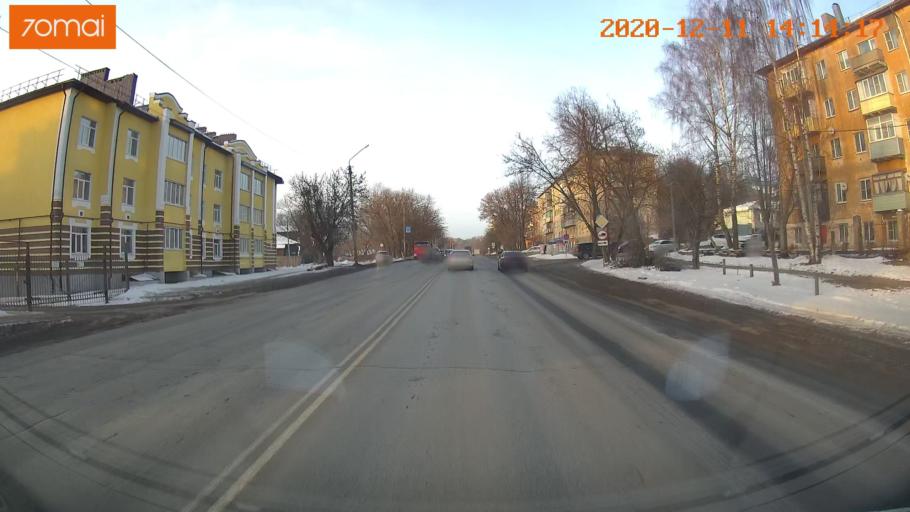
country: RU
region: Kostroma
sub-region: Kostromskoy Rayon
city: Kostroma
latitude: 57.7516
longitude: 40.9526
